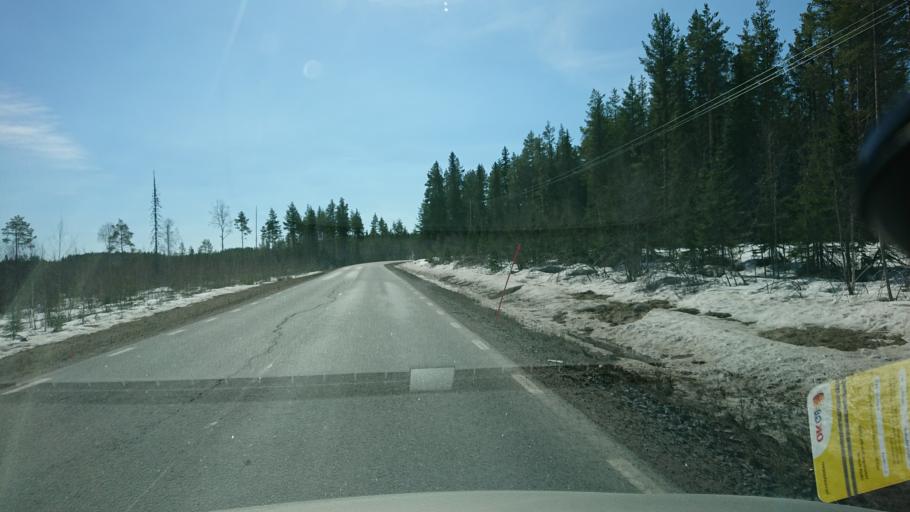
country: SE
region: Vaesternorrland
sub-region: Solleftea Kommun
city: As
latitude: 63.6137
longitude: 16.4376
